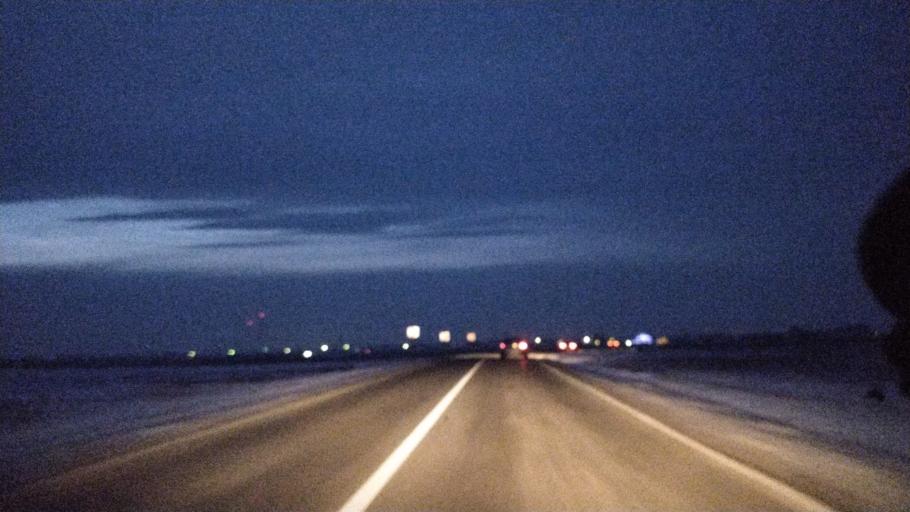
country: RO
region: Vrancea
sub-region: Comuna Milcovul
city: Milcovul
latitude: 45.6745
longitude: 27.2540
